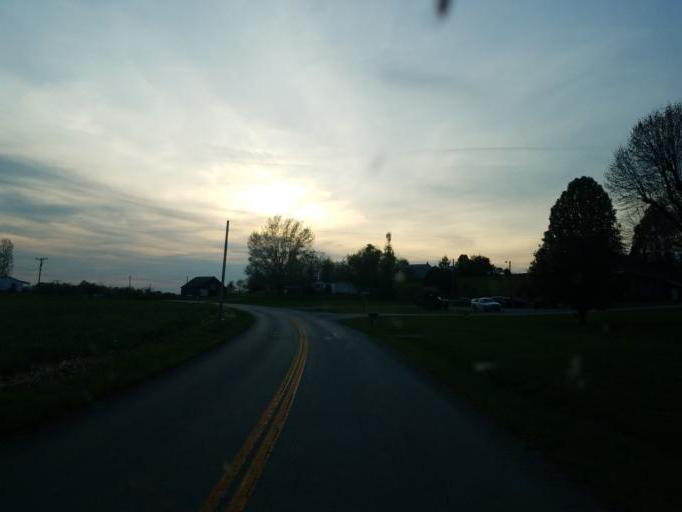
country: US
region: Kentucky
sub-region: Hart County
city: Munfordville
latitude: 37.2335
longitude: -85.7021
